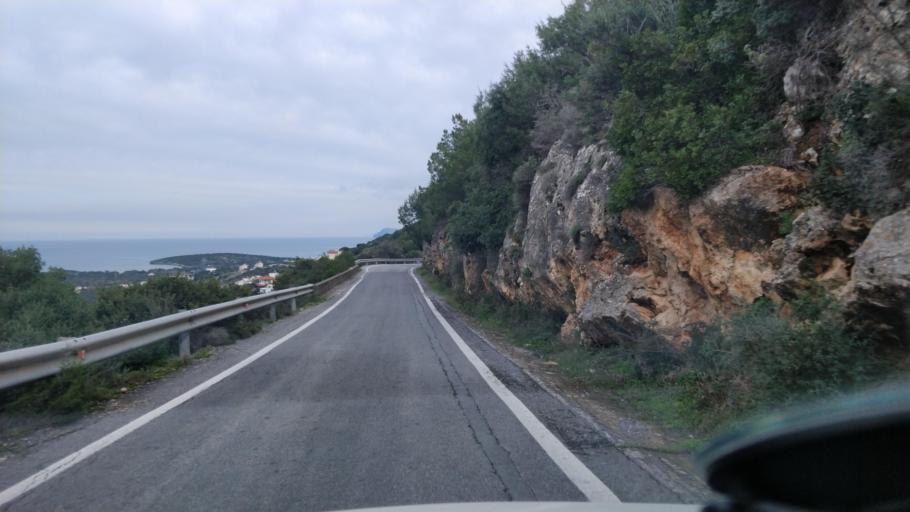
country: GR
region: Crete
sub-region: Nomos Lasithiou
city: Agios Nikolaos
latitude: 35.1108
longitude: 25.7176
